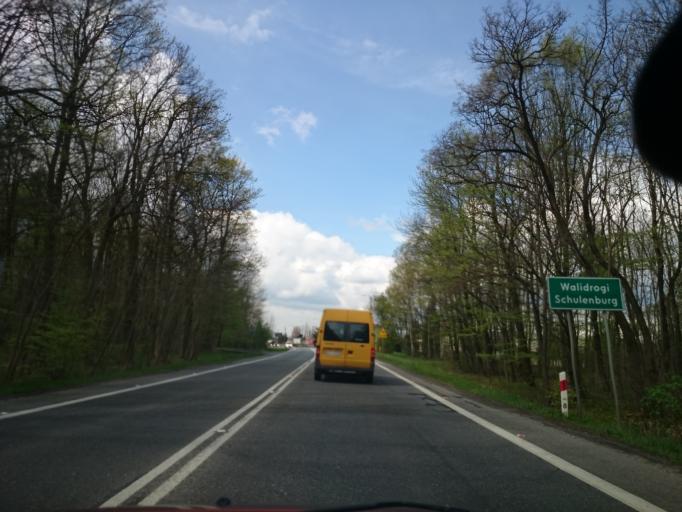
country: PL
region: Opole Voivodeship
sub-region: Powiat opolski
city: Tarnow Opolski
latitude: 50.5987
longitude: 18.0874
